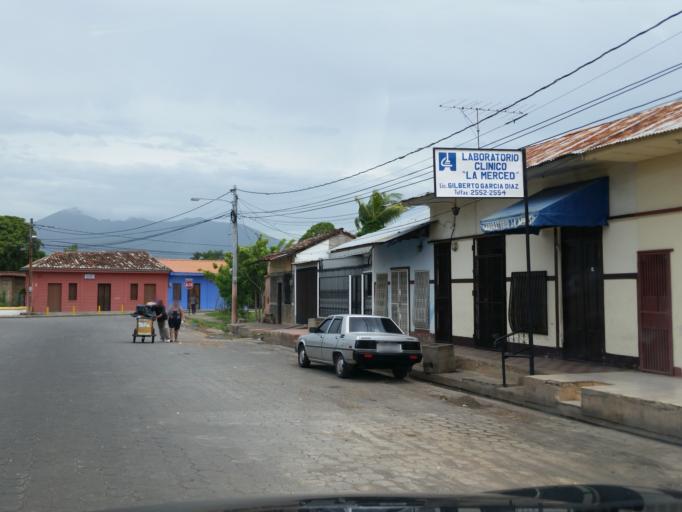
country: NI
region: Granada
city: Granada
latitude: 11.9338
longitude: -85.9573
